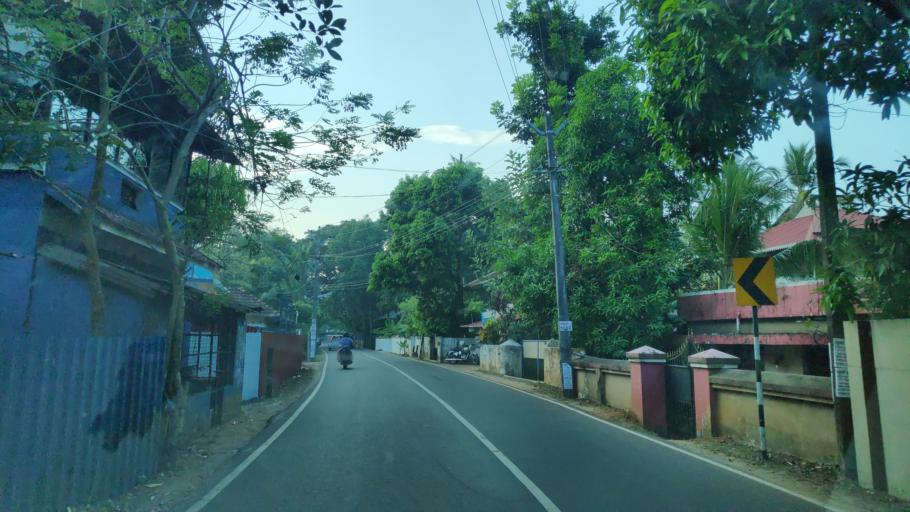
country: IN
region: Kerala
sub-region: Alappuzha
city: Shertallai
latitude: 9.6775
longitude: 76.3921
